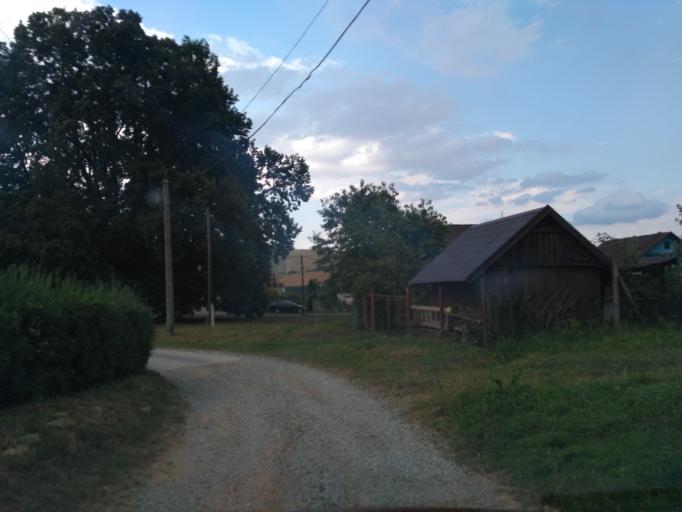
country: SK
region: Presovsky
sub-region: Okres Presov
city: Presov
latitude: 48.9247
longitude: 21.1859
